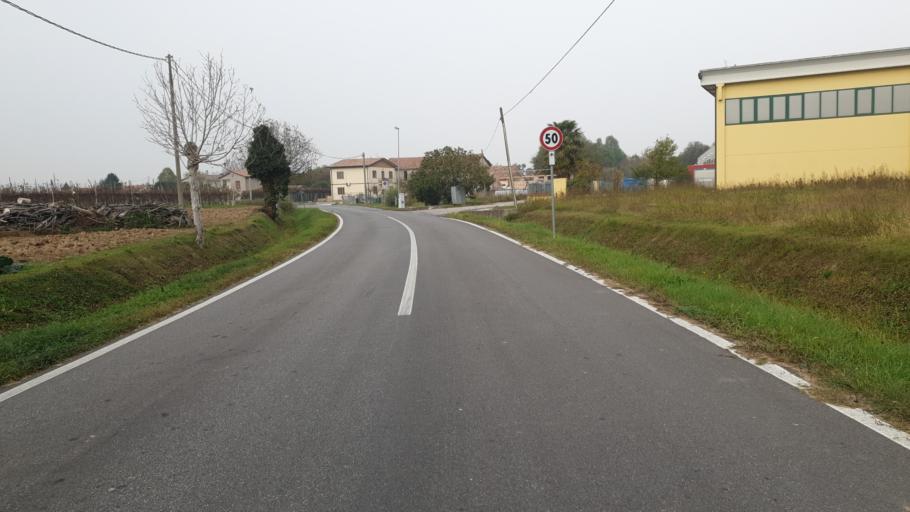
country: IT
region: Veneto
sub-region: Provincia di Padova
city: Bertipaglia
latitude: 45.3044
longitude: 11.8986
